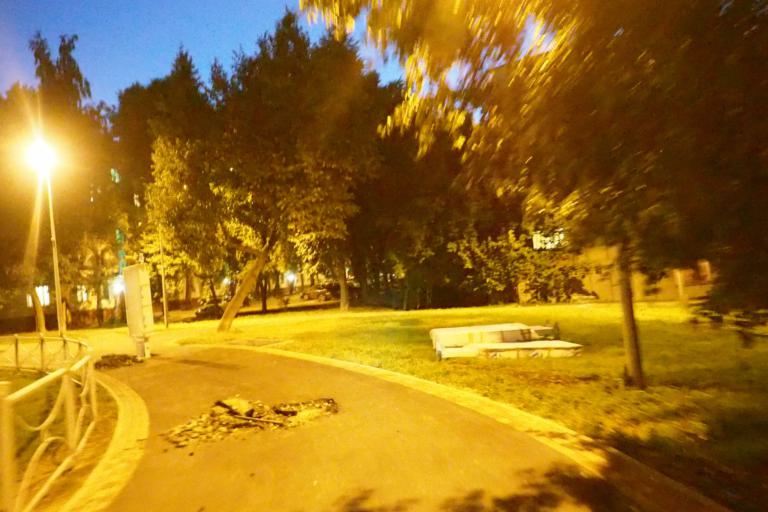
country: RU
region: Moscow
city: Zyuzino
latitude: 55.6591
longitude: 37.5768
